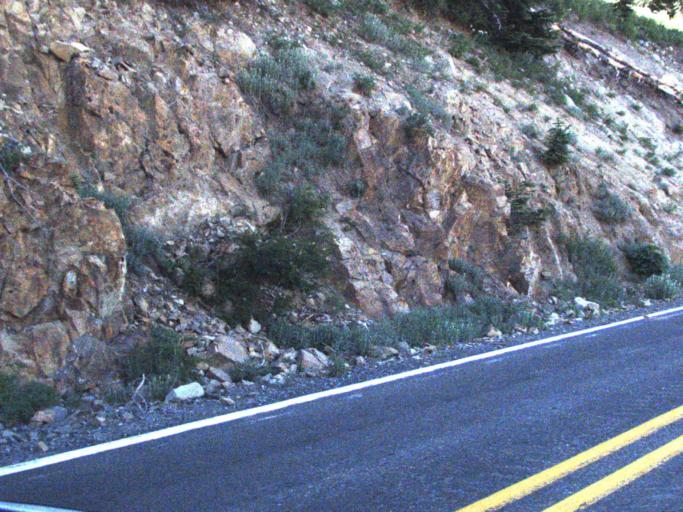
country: US
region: Washington
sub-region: King County
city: Enumclaw
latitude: 46.8703
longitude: -121.5148
